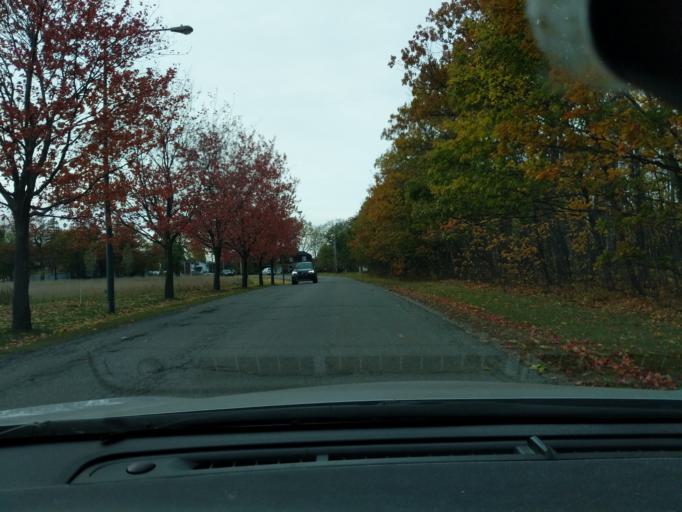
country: CA
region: Quebec
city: Quebec
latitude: 46.7754
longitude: -71.2519
